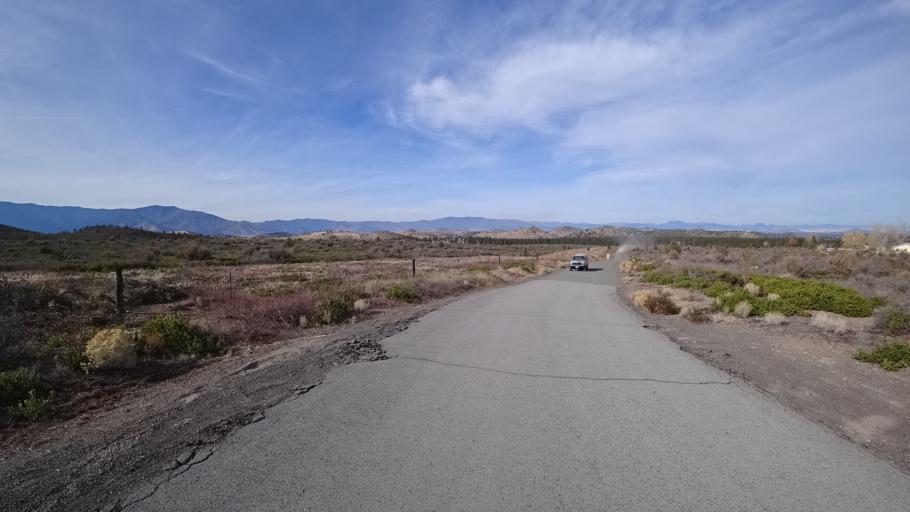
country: US
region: California
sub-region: Siskiyou County
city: Weed
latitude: 41.4814
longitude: -122.3632
